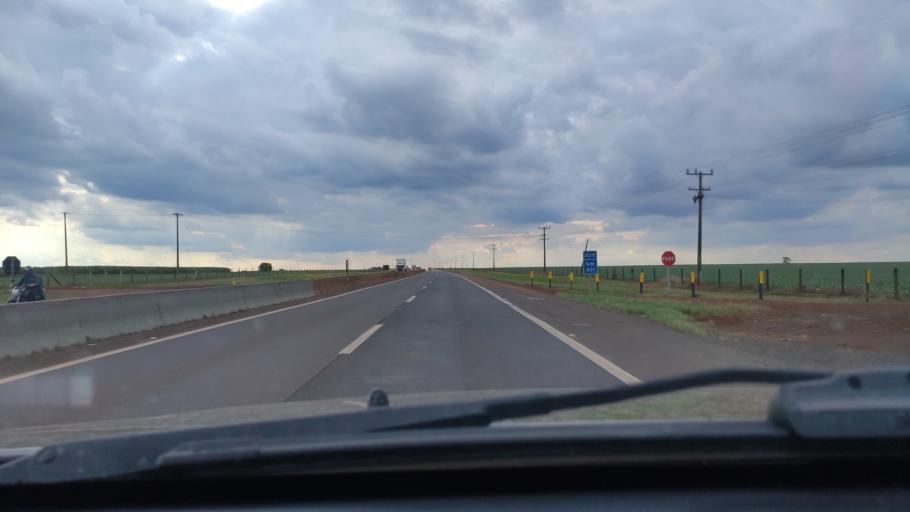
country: BR
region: Sao Paulo
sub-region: Palmital
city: Palmital
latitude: -22.8233
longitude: -50.0387
